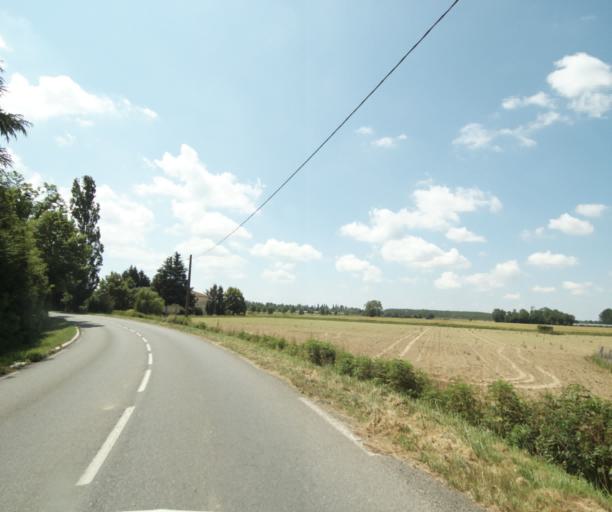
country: FR
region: Midi-Pyrenees
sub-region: Departement du Tarn-et-Garonne
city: Montauban
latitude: 44.0828
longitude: 1.3467
